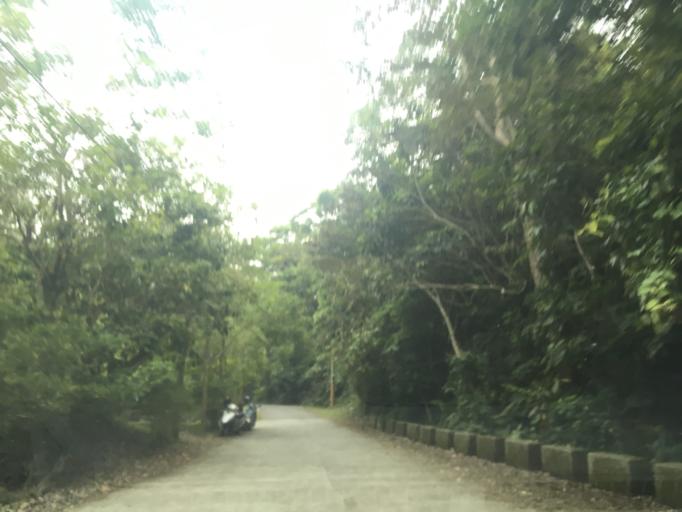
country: TW
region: Taiwan
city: Zhongxing New Village
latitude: 24.0495
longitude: 120.7827
